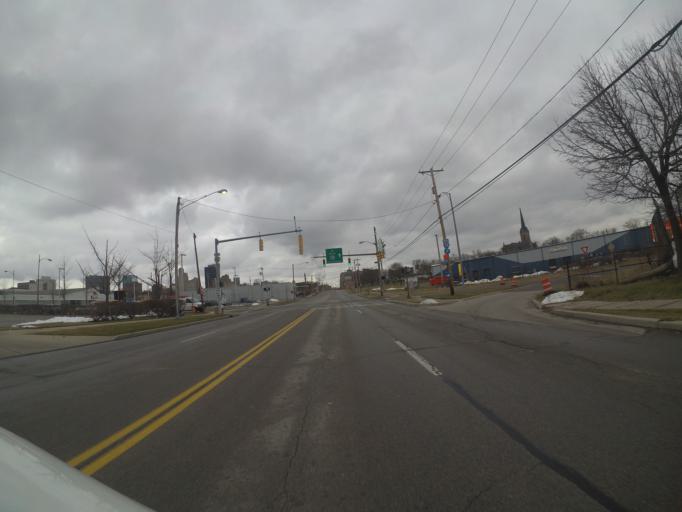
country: US
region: Ohio
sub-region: Lucas County
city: Toledo
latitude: 41.6519
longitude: -83.5477
